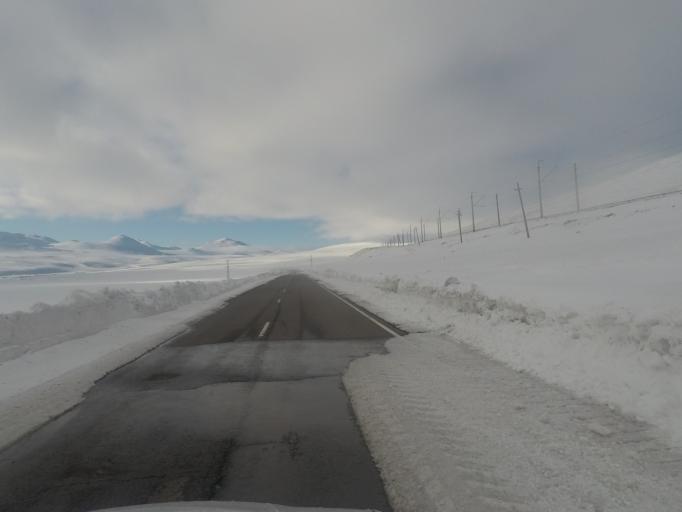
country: GE
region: Kvemo Kartli
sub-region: Tsalka
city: Tsalka
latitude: 41.4705
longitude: 43.8550
